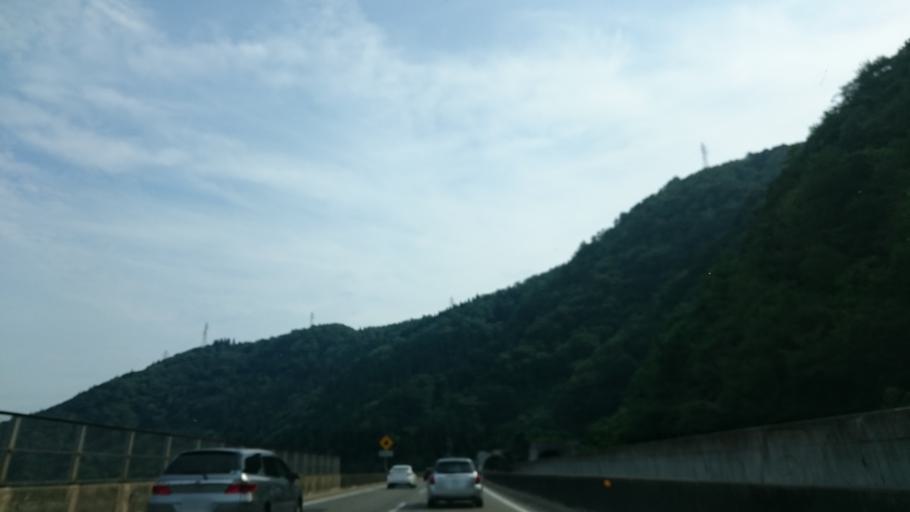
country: JP
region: Gifu
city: Gujo
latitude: 35.7423
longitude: 136.9446
